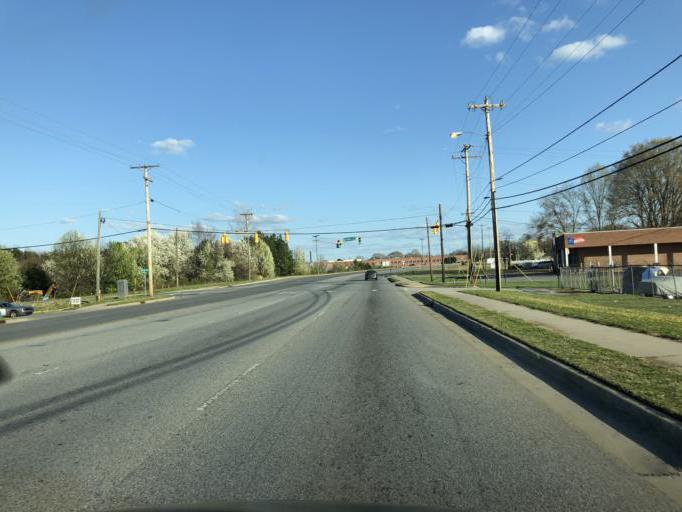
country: US
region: North Carolina
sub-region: Gaston County
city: Gastonia
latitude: 35.2740
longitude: -81.2259
